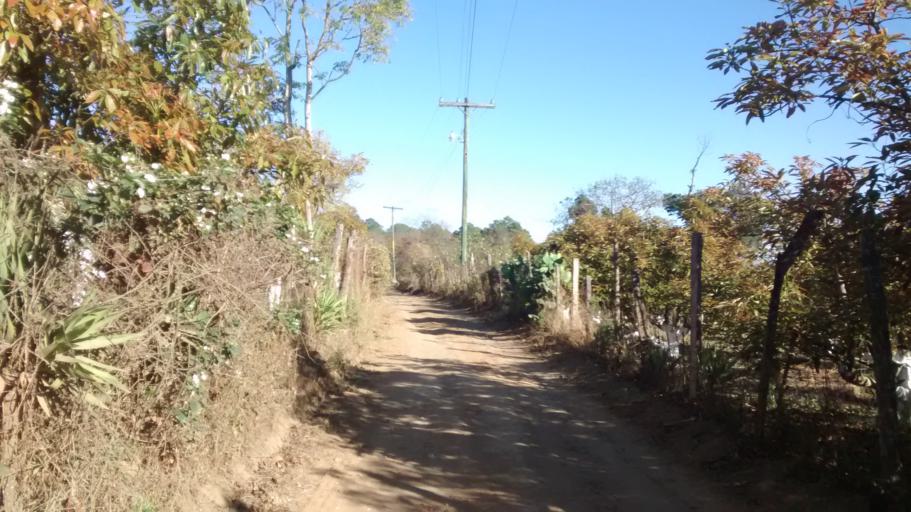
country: GT
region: Sacatepequez
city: Santo Domingo Xenacoj
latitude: 14.6716
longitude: -90.7203
